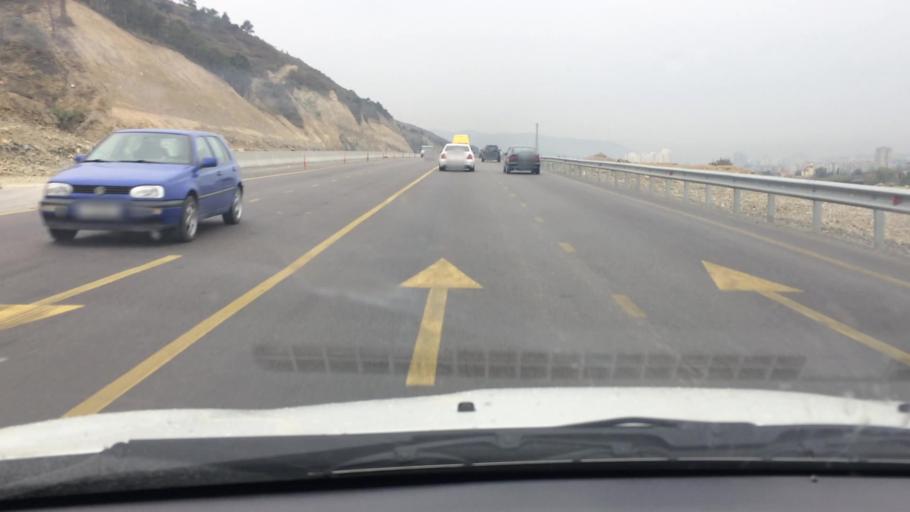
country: GE
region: T'bilisi
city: Tbilisi
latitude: 41.6621
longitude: 44.8824
